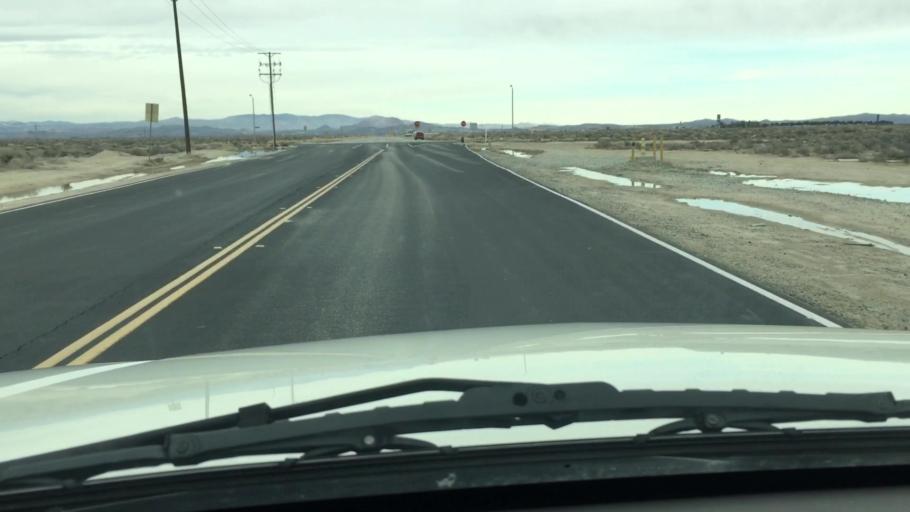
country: US
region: California
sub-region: Los Angeles County
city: Lancaster
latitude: 34.7317
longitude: -118.1840
